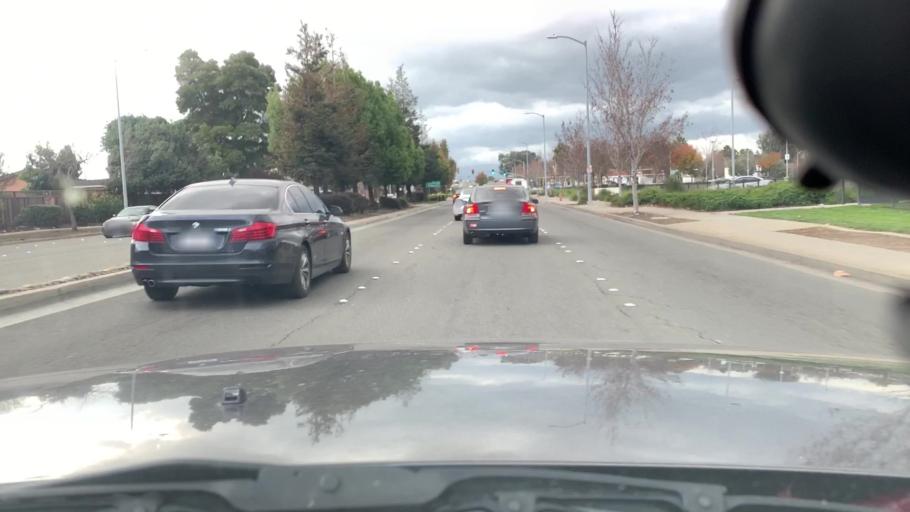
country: US
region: California
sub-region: Alameda County
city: Fremont
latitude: 37.5277
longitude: -121.9837
